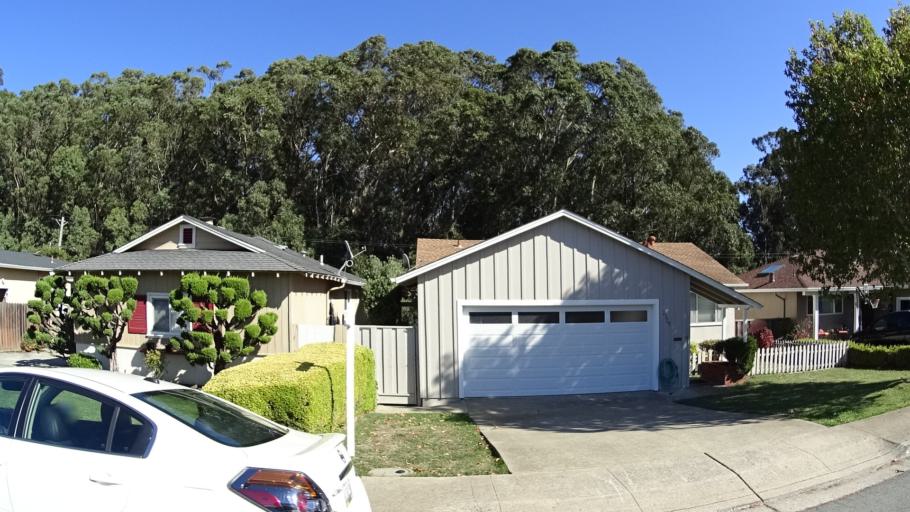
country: US
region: California
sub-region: San Mateo County
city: San Bruno
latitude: 37.6231
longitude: -122.4314
